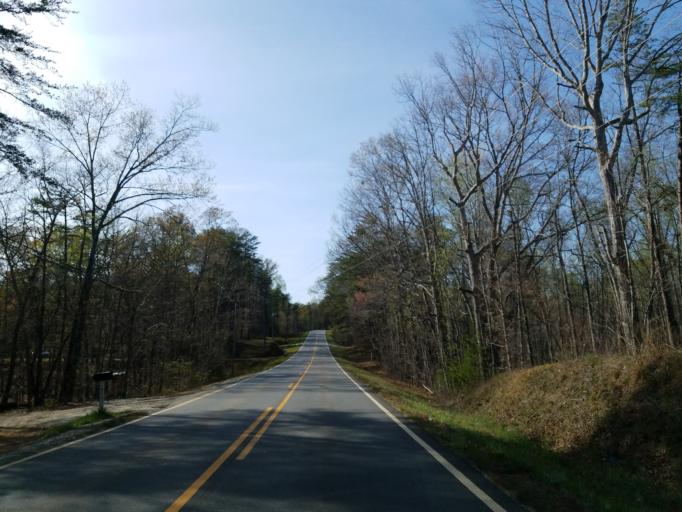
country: US
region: Georgia
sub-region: Lumpkin County
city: Dahlonega
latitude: 34.4531
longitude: -84.0193
